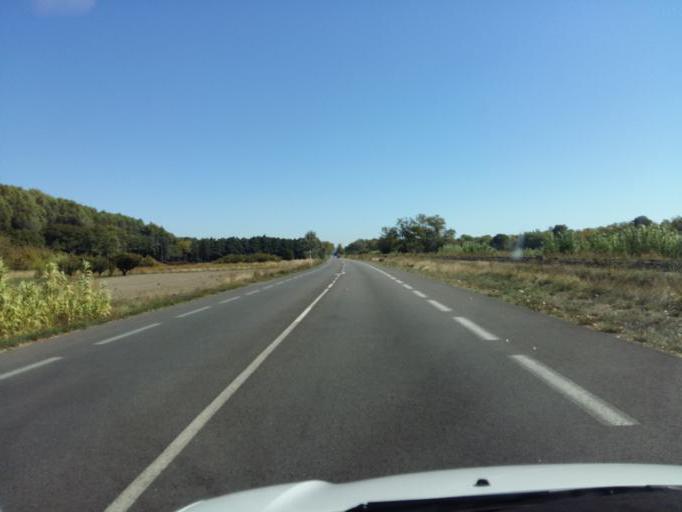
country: FR
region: Provence-Alpes-Cote d'Azur
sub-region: Departement du Vaucluse
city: Merindol
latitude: 43.7548
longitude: 5.2363
